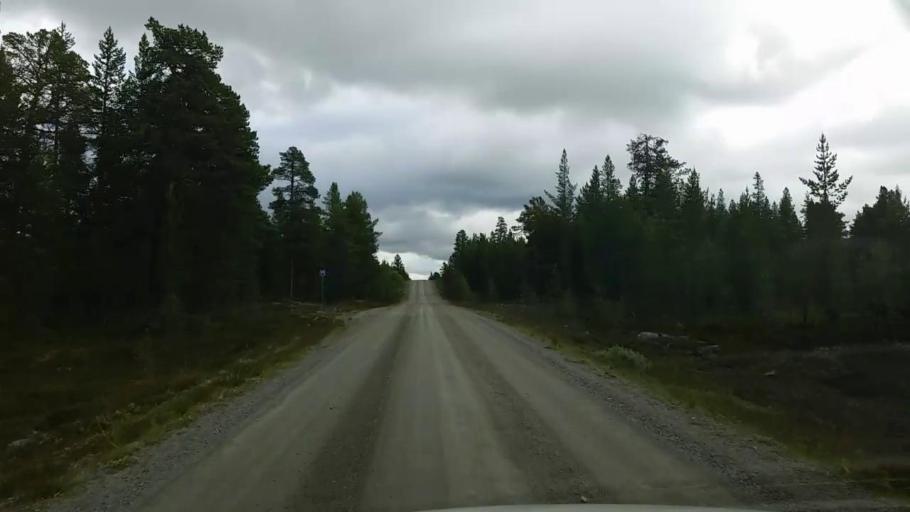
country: NO
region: Hedmark
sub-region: Engerdal
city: Engerdal
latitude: 62.3400
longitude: 12.6149
